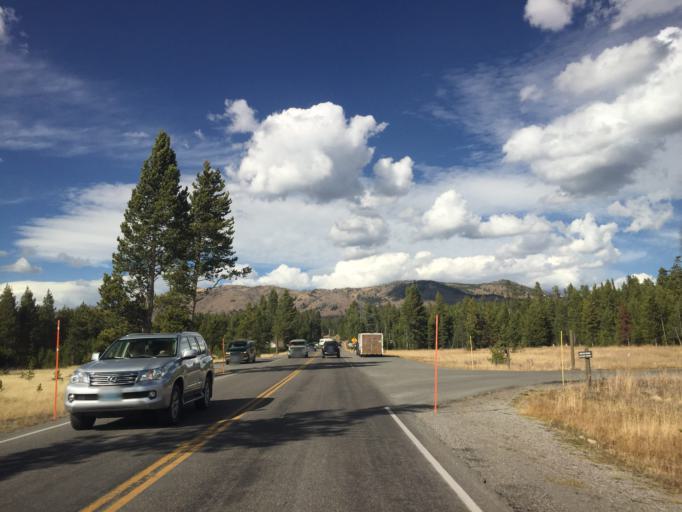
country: US
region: Montana
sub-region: Gallatin County
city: West Yellowstone
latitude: 44.7336
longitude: -110.4934
